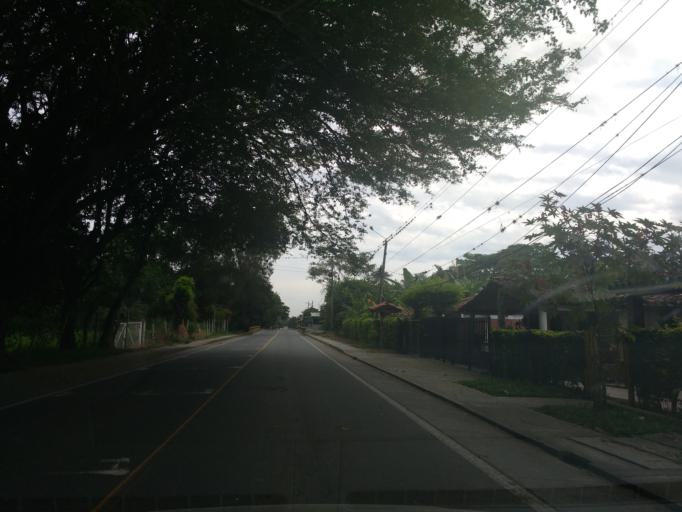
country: CO
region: Cauca
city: Miranda
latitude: 3.2810
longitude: -76.2231
